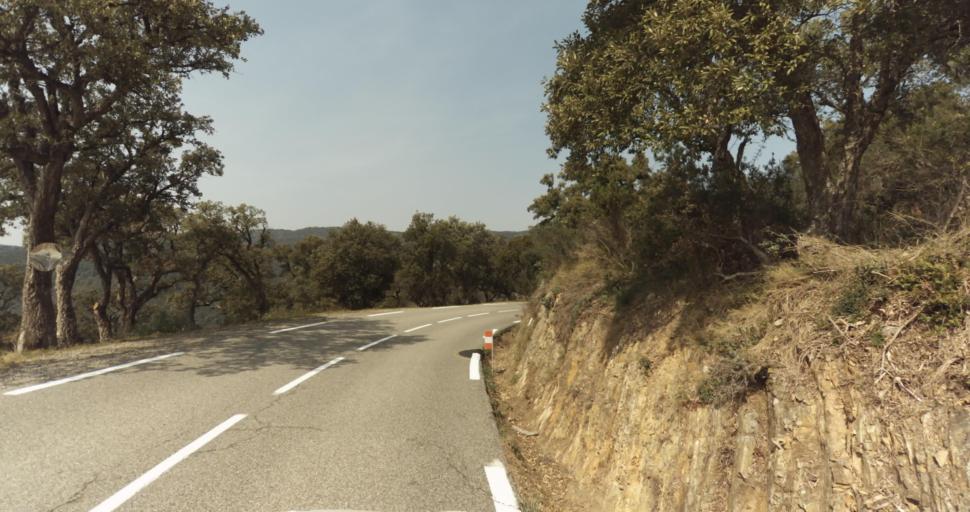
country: FR
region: Provence-Alpes-Cote d'Azur
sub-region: Departement du Var
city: Bormes-les-Mimosas
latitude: 43.1655
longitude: 6.3314
